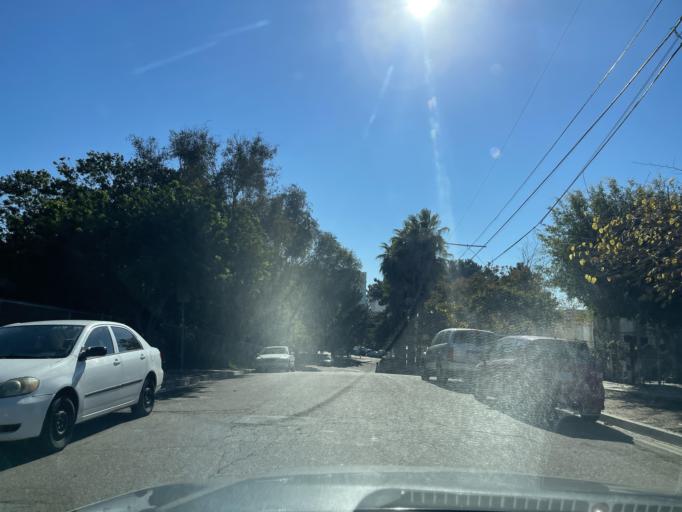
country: US
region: California
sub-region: San Diego County
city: National City
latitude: 32.6746
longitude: -117.1008
